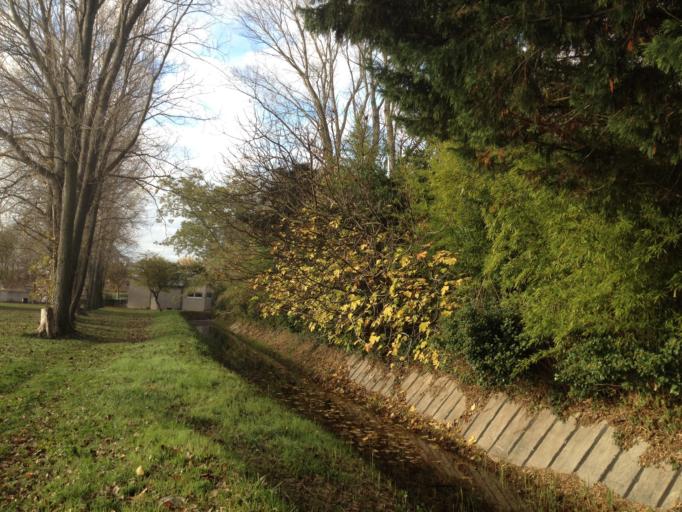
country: FR
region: Provence-Alpes-Cote d'Azur
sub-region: Departement du Vaucluse
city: Orange
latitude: 44.1305
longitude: 4.8300
